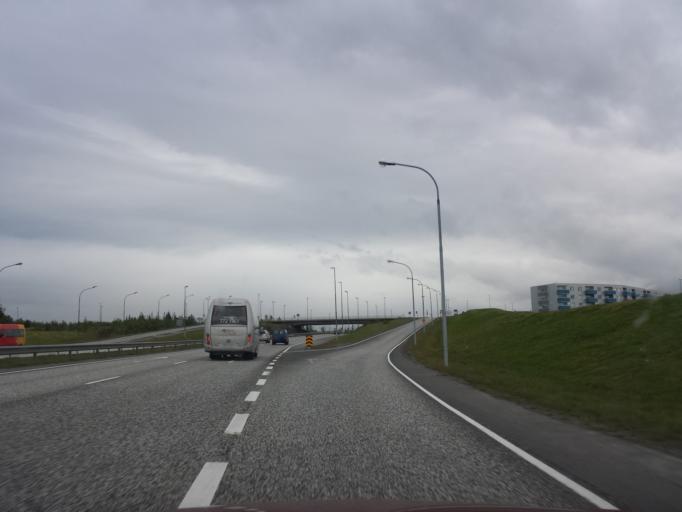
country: IS
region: Capital Region
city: Gardabaer
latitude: 64.0977
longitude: -21.9193
